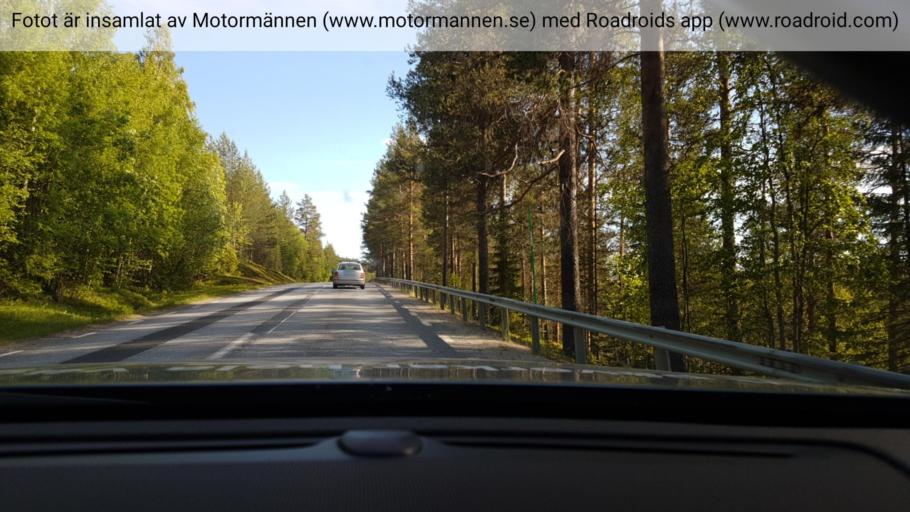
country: SE
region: Vaesterbotten
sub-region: Vindelns Kommun
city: Vindeln
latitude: 64.2715
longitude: 19.6340
